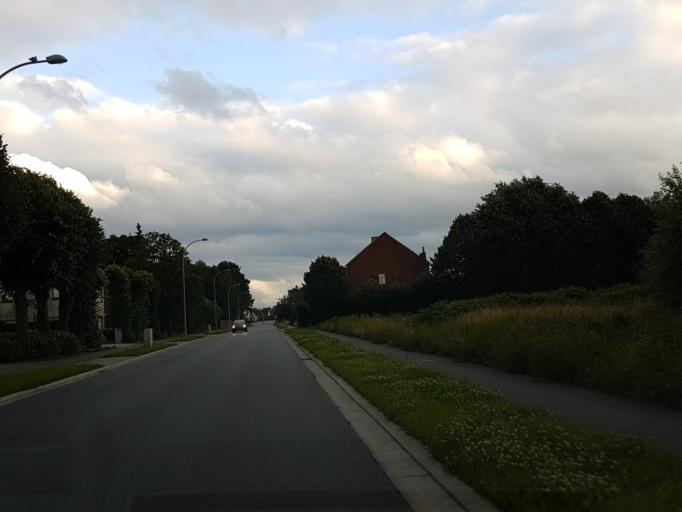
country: BE
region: Flanders
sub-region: Provincie Oost-Vlaanderen
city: Buggenhout
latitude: 50.9920
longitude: 4.2132
